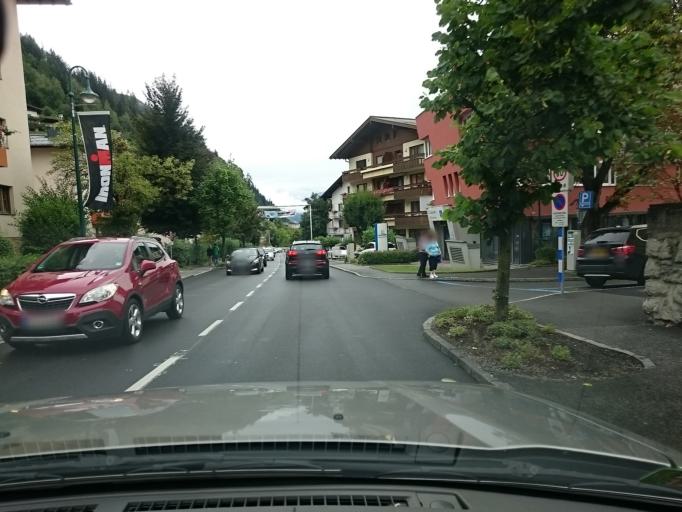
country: AT
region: Salzburg
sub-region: Politischer Bezirk Zell am See
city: Zell am See
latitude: 47.3266
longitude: 12.7966
